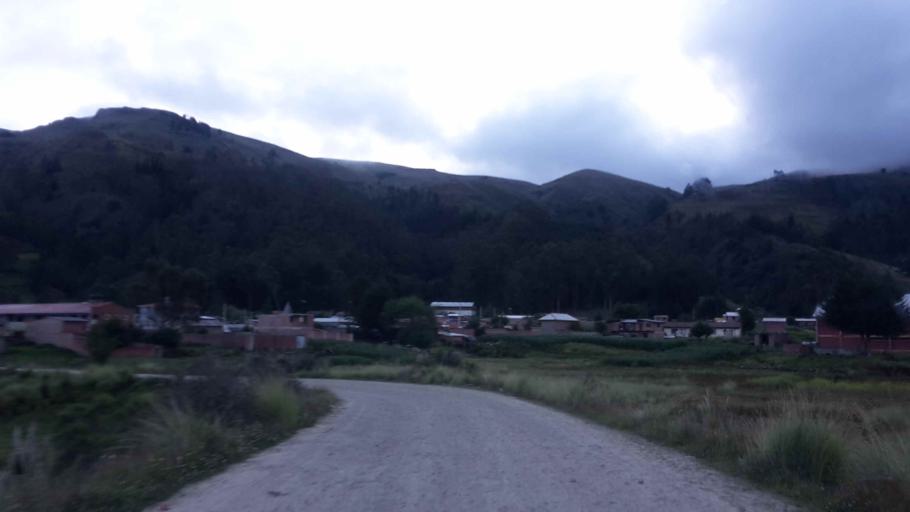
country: BO
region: Cochabamba
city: Colomi
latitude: -17.2728
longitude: -65.9242
